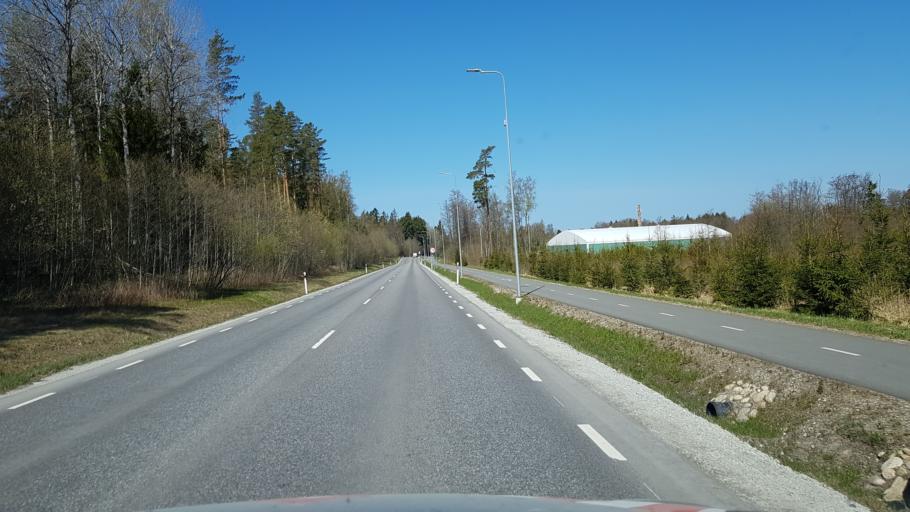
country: EE
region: Harju
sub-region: Viimsi vald
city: Viimsi
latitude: 59.5256
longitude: 24.8834
